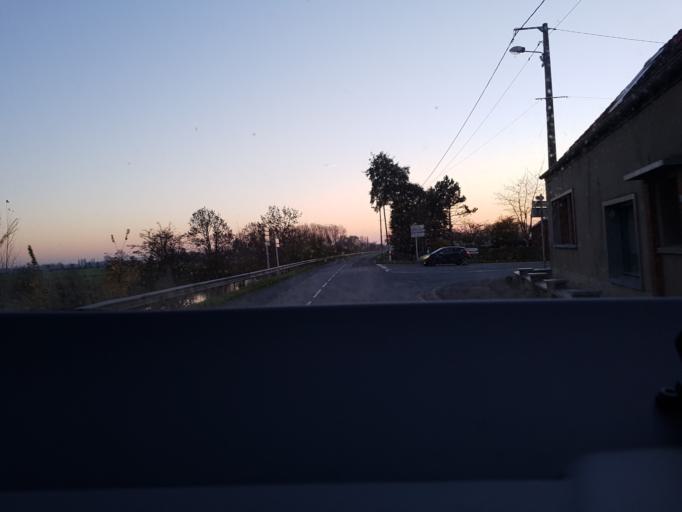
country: FR
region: Nord-Pas-de-Calais
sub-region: Departement du Nord
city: Spycker
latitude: 50.9568
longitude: 2.3204
